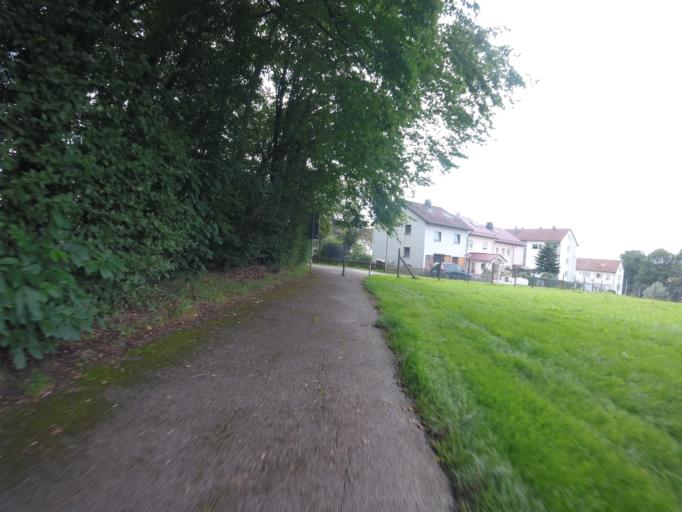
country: DE
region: Baden-Wuerttemberg
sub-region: Regierungsbezirk Stuttgart
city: Backnang
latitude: 48.9454
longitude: 9.4635
